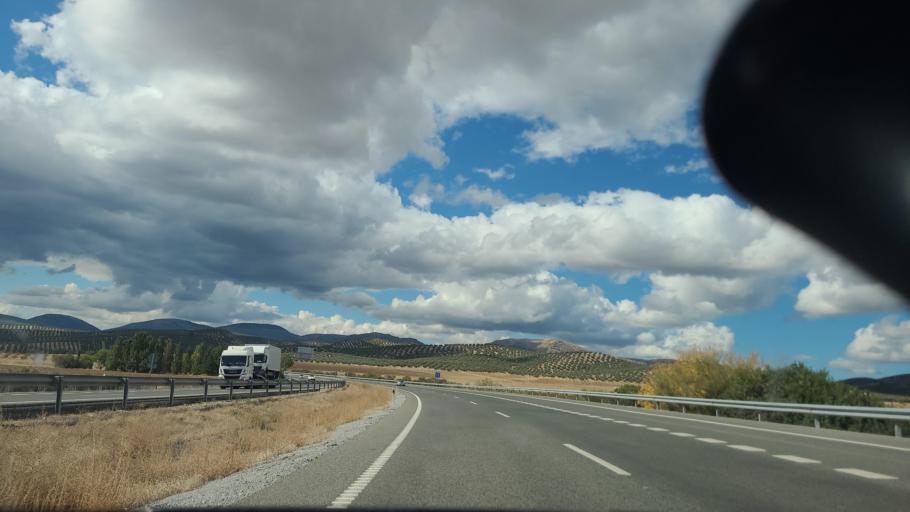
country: ES
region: Andalusia
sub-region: Provincia de Granada
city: Campotejar
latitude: 37.4885
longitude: -3.6069
